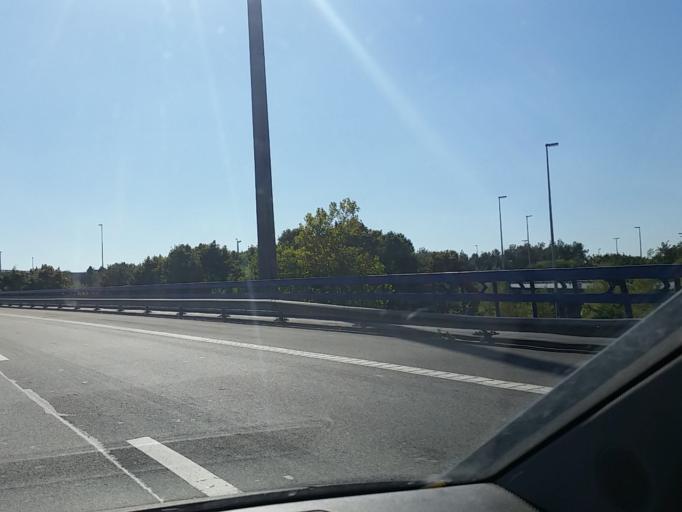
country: BE
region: Flanders
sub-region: Provincie Vlaams-Brabant
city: Dilbeek
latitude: 50.8238
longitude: 4.2800
